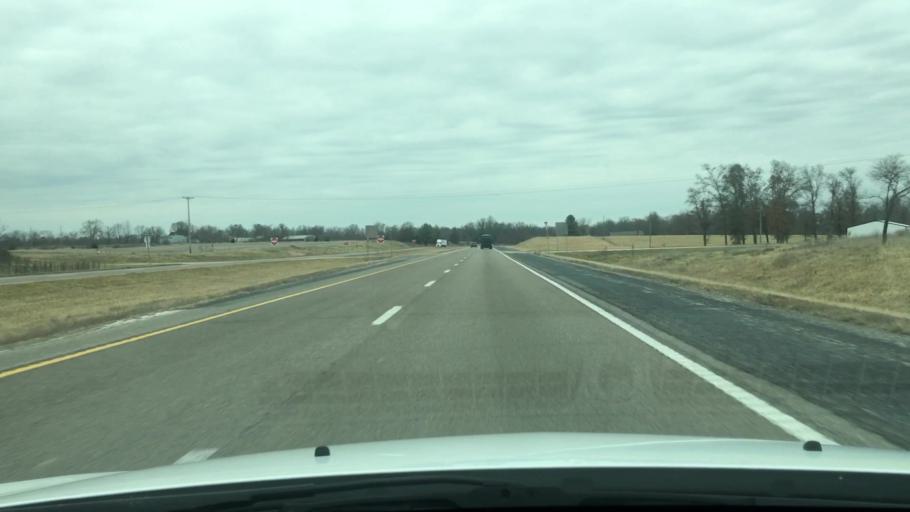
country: US
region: Missouri
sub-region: Audrain County
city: Mexico
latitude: 39.0370
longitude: -91.8904
